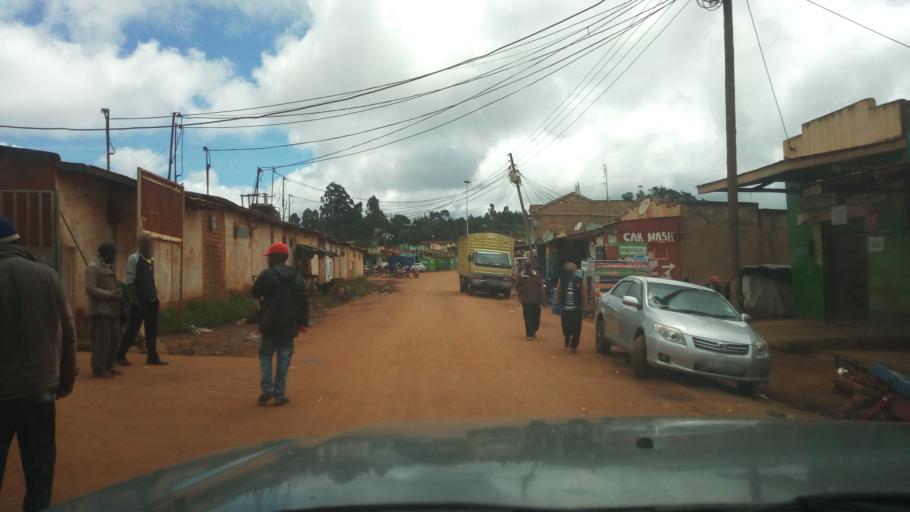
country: KE
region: Makueni
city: Wote
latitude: -1.6625
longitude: 37.4470
